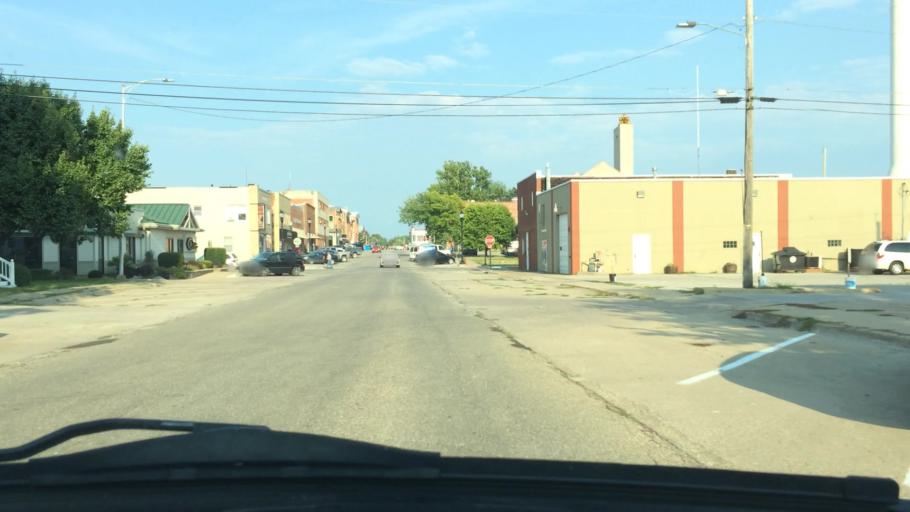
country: US
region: Iowa
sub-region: Henry County
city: Mount Pleasant
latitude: 40.9669
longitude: -91.5569
